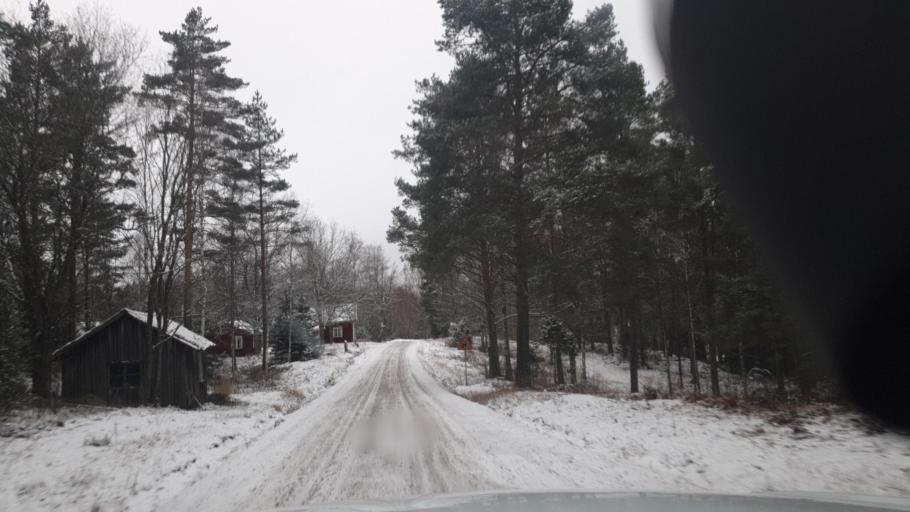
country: SE
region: Vaermland
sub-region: Karlstads Kommun
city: Edsvalla
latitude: 59.6233
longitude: 13.0633
